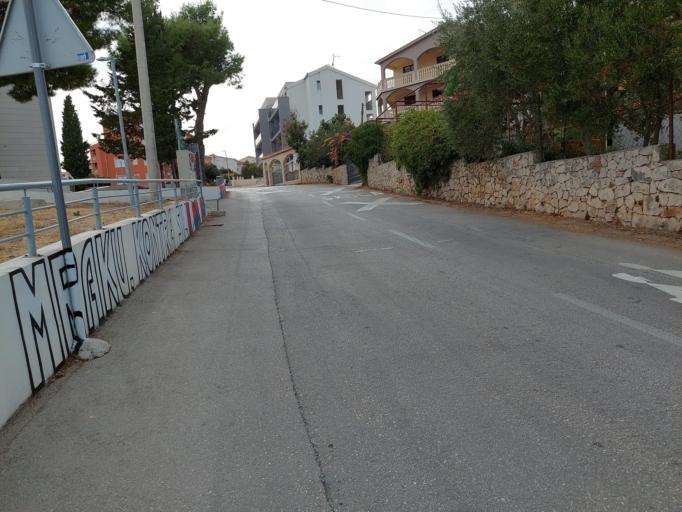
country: HR
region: Splitsko-Dalmatinska
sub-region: Grad Trogir
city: Trogir
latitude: 43.4924
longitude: 16.2702
